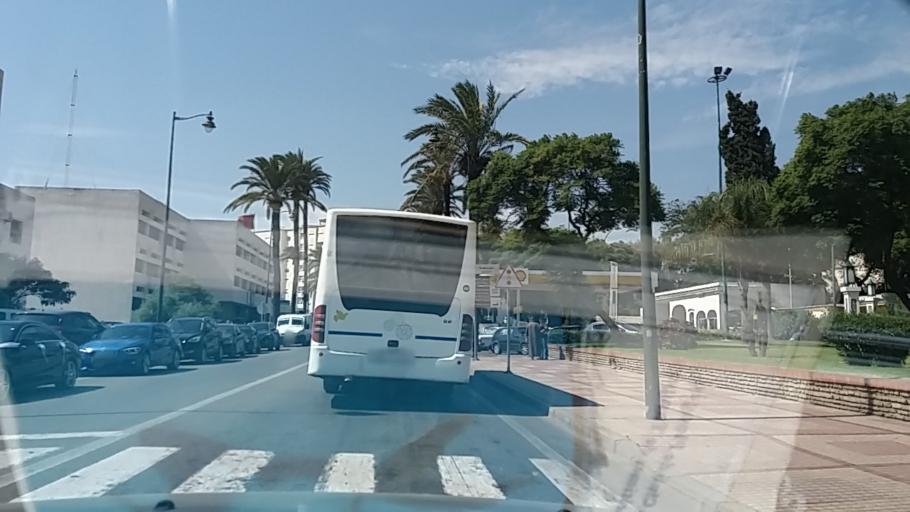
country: MA
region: Tanger-Tetouan
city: Tetouan
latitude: 35.5681
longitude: -5.3784
